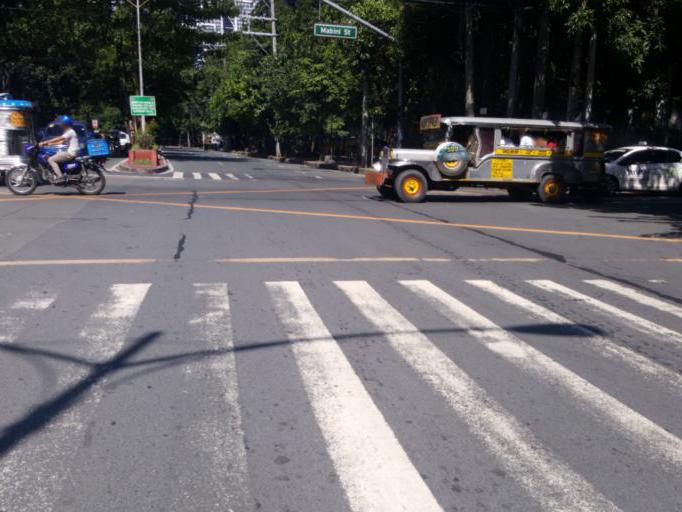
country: PH
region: Metro Manila
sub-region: City of Manila
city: Port Area
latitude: 14.5650
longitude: 120.9866
